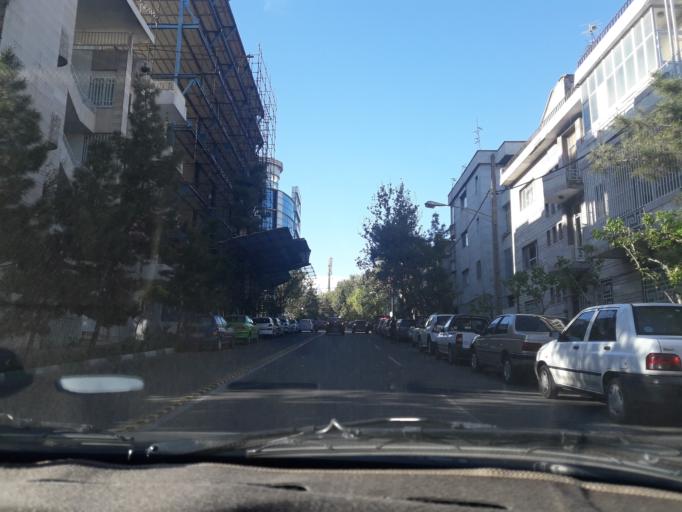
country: IR
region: Tehran
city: Tehran
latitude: 35.7217
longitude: 51.4025
